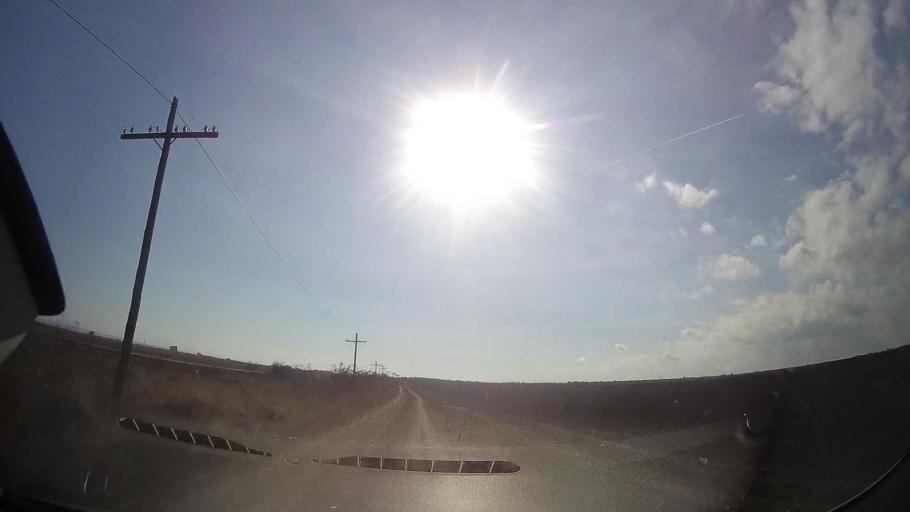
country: RO
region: Constanta
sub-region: Comuna Tuzla
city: Tuzla
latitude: 43.9828
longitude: 28.6446
